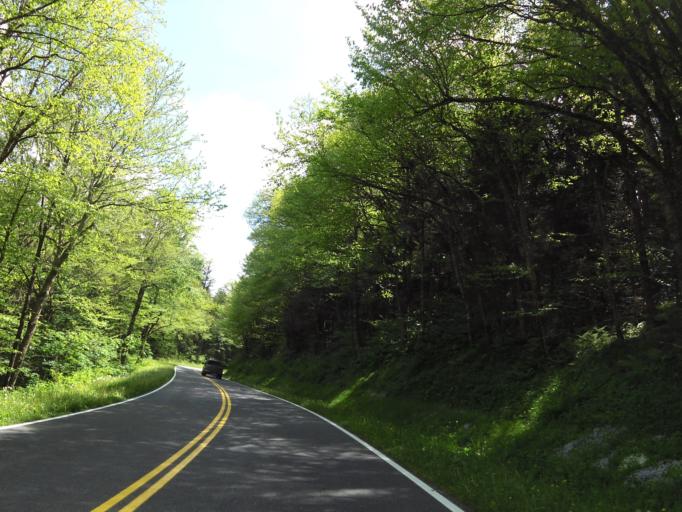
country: US
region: Tennessee
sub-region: Sevier County
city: Gatlinburg
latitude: 35.6074
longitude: -83.4479
